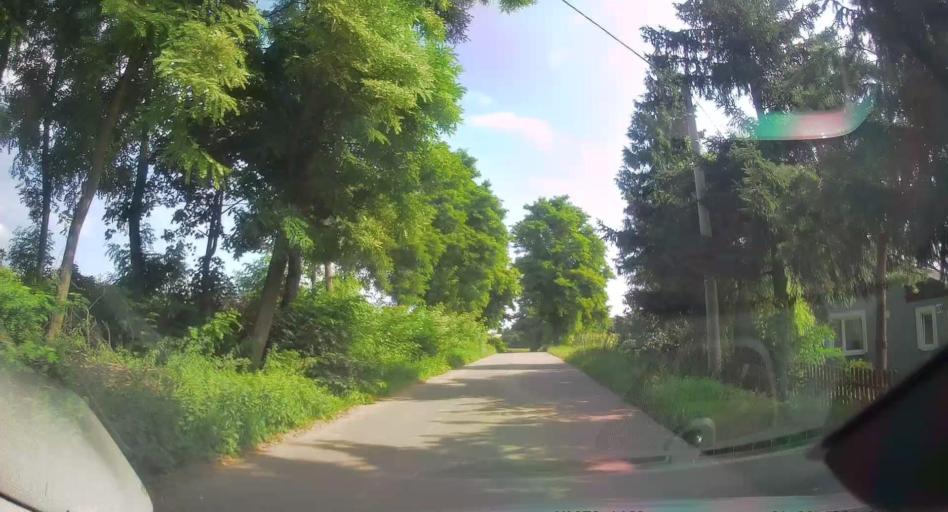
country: PL
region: Lesser Poland Voivodeship
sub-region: Powiat proszowicki
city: Nowe Brzesko
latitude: 50.1513
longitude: 20.4396
